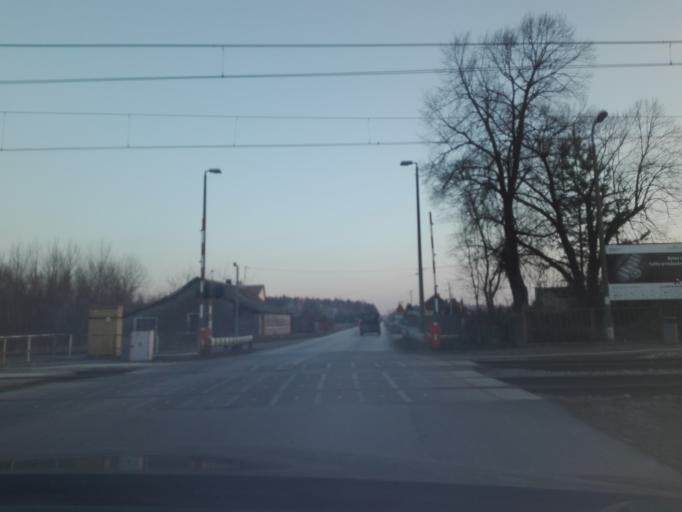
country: PL
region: Subcarpathian Voivodeship
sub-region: Powiat tarnobrzeski
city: Sokolniki
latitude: 50.6043
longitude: 21.8374
